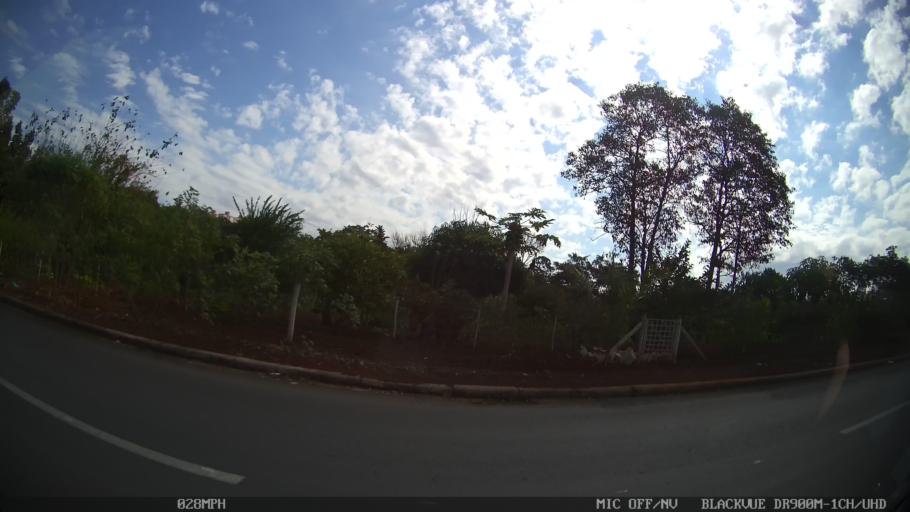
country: BR
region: Sao Paulo
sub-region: Americana
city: Americana
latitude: -22.7242
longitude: -47.3279
